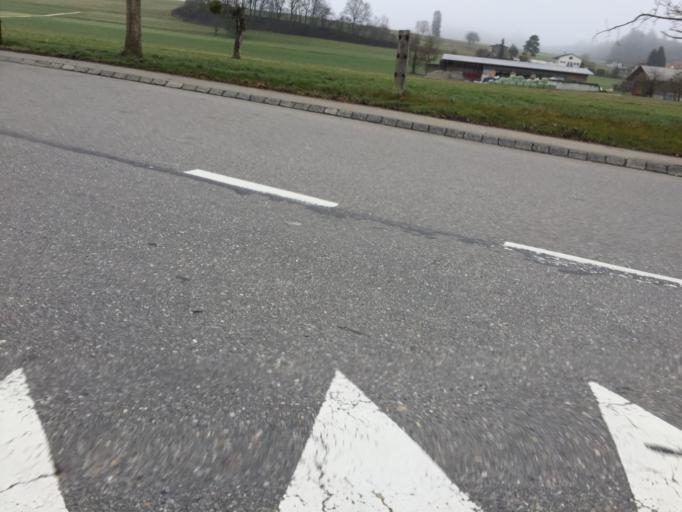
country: CH
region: Bern
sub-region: Seeland District
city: Grossaffoltern
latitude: 47.1069
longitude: 7.3460
